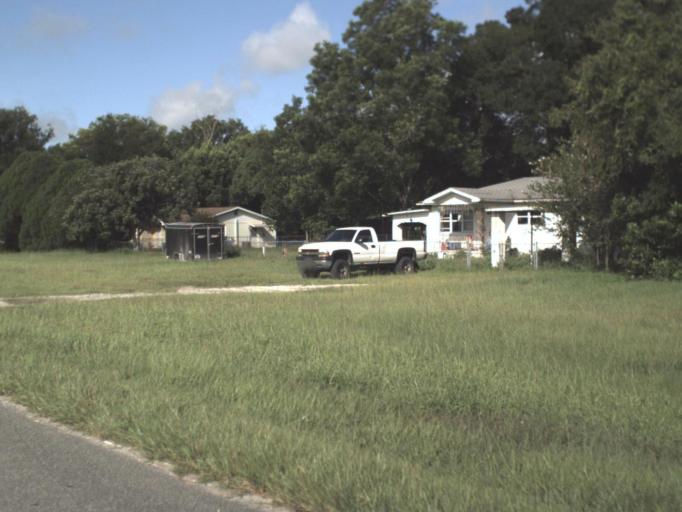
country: US
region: Florida
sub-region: Hernando County
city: Masaryktown
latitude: 28.4324
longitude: -82.4627
